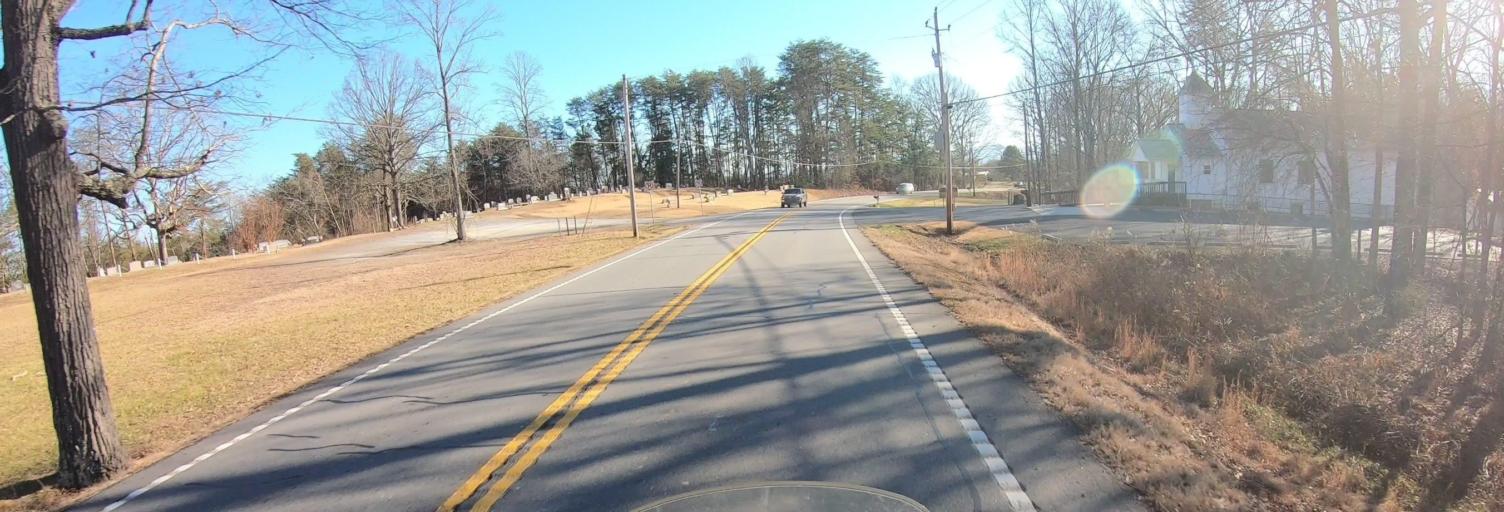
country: US
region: Georgia
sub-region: Fannin County
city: McCaysville
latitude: 34.9533
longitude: -84.3174
